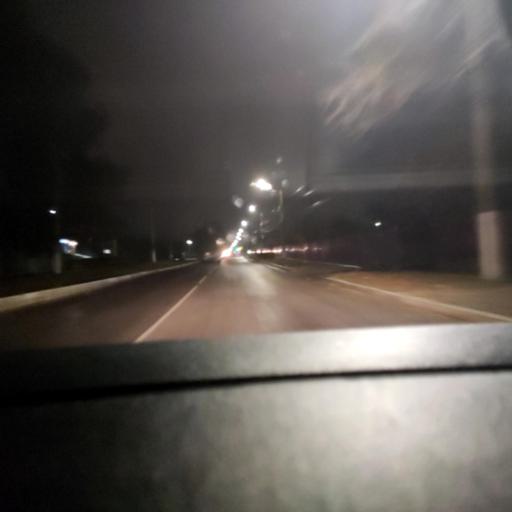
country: RU
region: Voronezj
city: Semiluki
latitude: 51.6924
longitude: 39.0343
